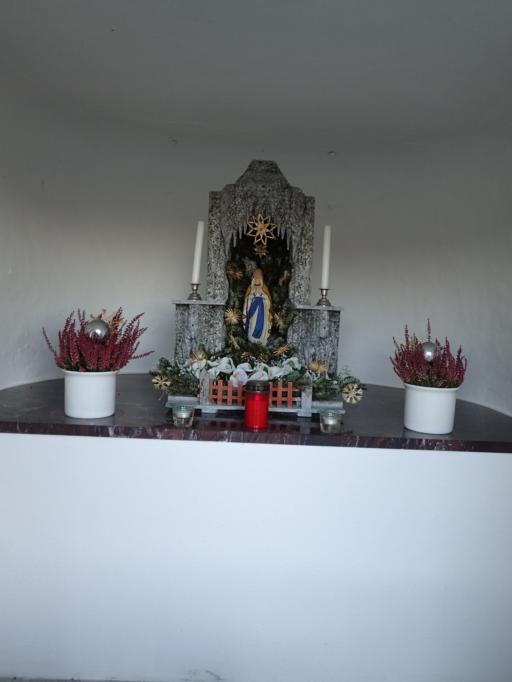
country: AT
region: Salzburg
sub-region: Politischer Bezirk Salzburg-Umgebung
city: Mattsee
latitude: 47.9601
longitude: 13.1207
